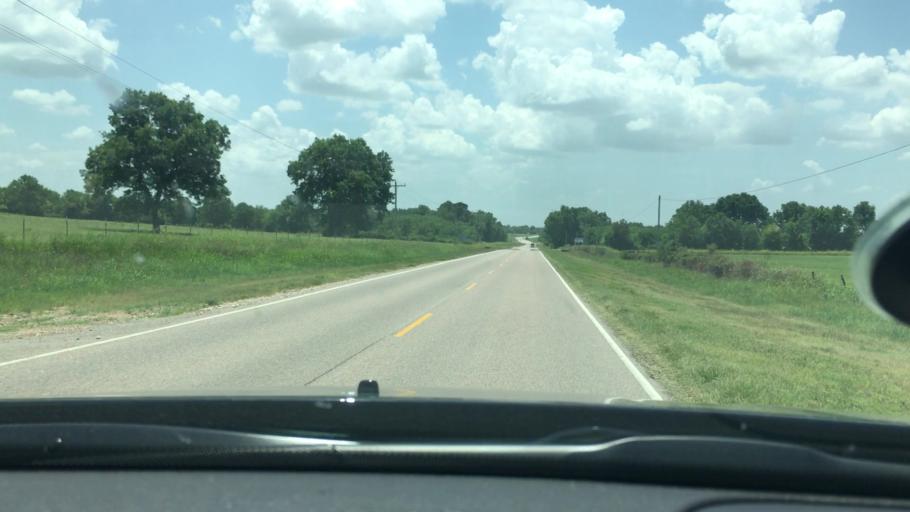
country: US
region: Oklahoma
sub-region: Johnston County
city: Tishomingo
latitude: 34.4656
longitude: -96.6360
